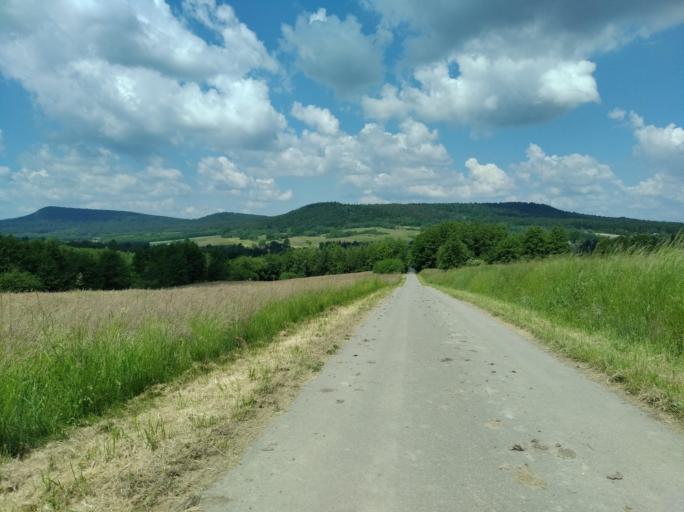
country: PL
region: Subcarpathian Voivodeship
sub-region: Powiat strzyzowski
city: Jawornik
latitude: 49.7830
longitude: 21.8688
